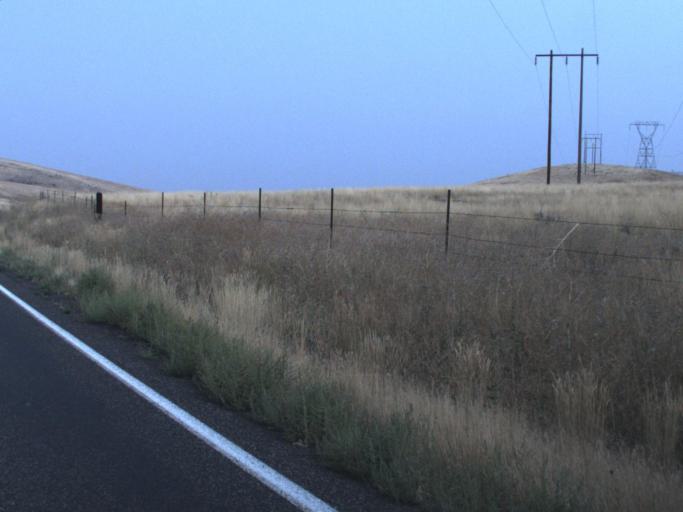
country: US
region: Washington
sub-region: Yakima County
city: Sunnyside
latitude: 46.4736
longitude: -119.9311
